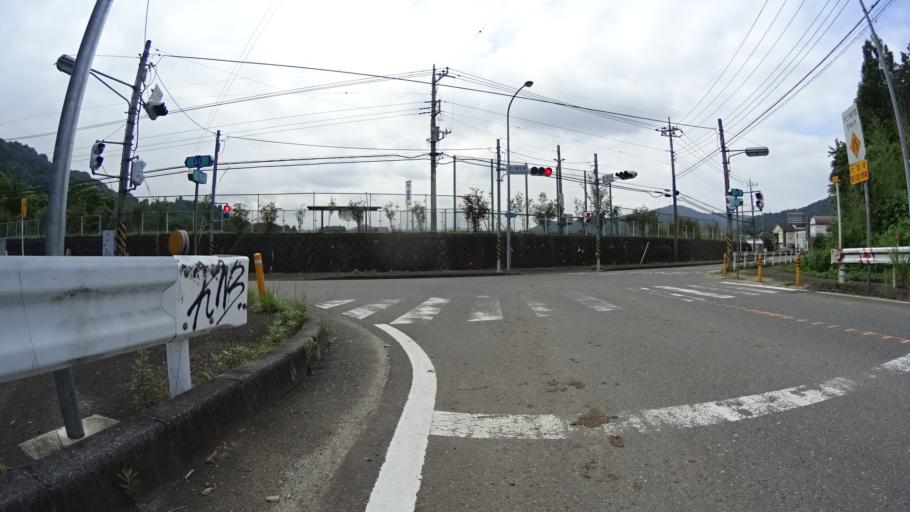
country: JP
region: Kanagawa
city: Hadano
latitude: 35.5185
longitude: 139.2309
